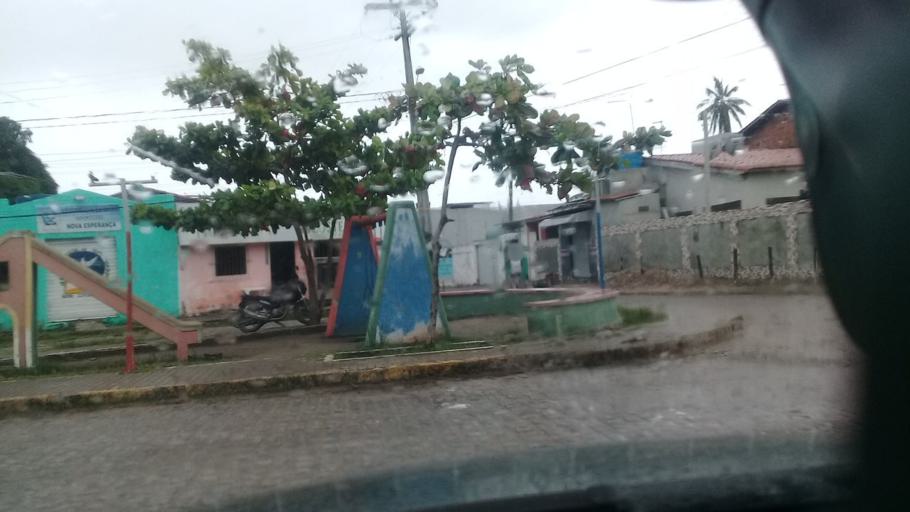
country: BR
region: Pernambuco
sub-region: Itamaraca
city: Itamaraca
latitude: -7.7470
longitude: -34.8265
